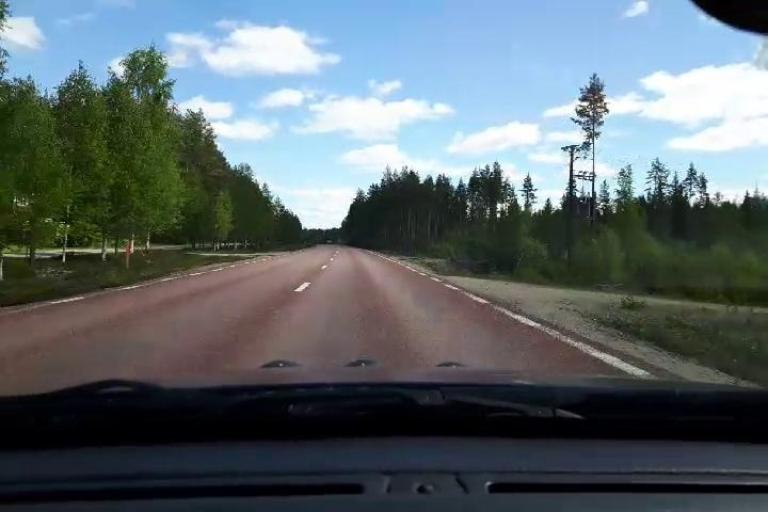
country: SE
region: Gaevleborg
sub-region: Ljusdals Kommun
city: Farila
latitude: 61.9306
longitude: 15.5430
